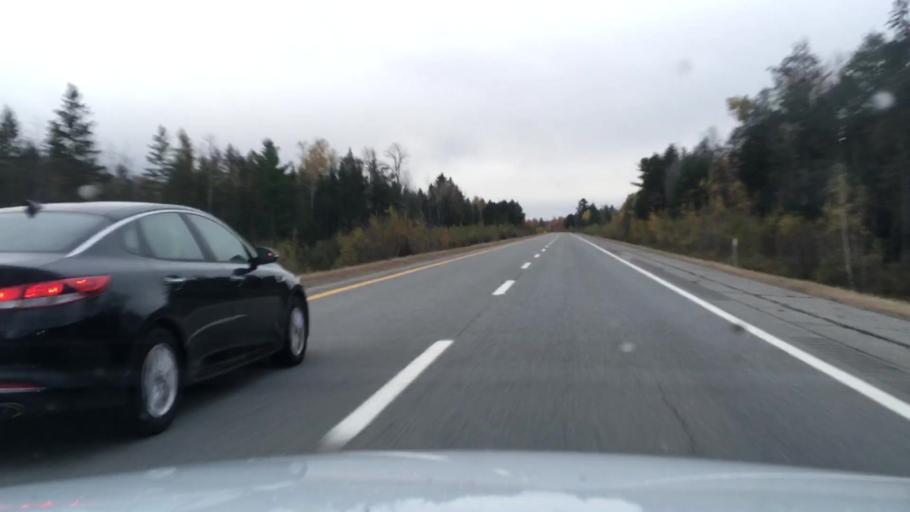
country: US
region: Maine
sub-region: Penobscot County
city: Greenbush
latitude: 45.1069
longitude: -68.6957
